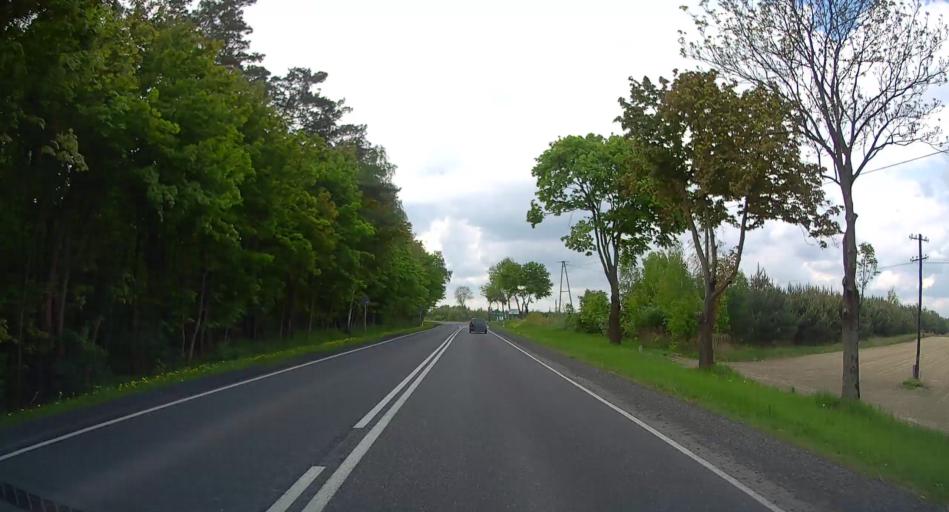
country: PL
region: Masovian Voivodeship
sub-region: Powiat nowodworski
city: Zakroczym
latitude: 52.4460
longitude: 20.5810
